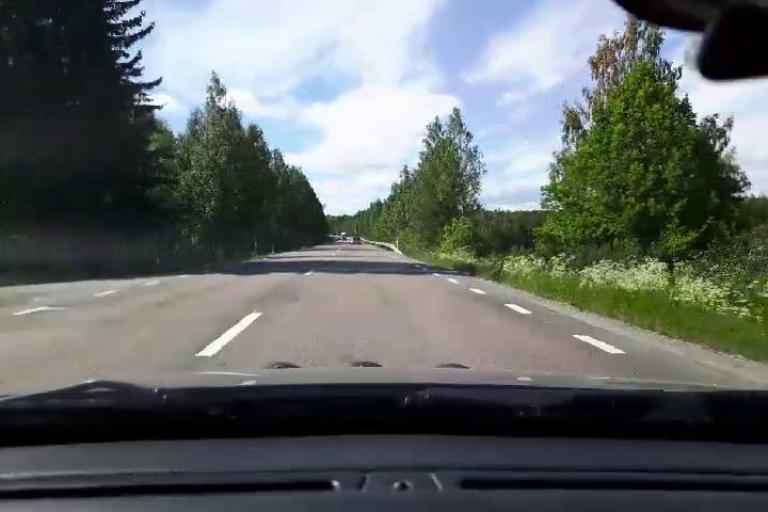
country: SE
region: Gaevleborg
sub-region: Bollnas Kommun
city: Kilafors
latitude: 61.2944
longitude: 16.4948
